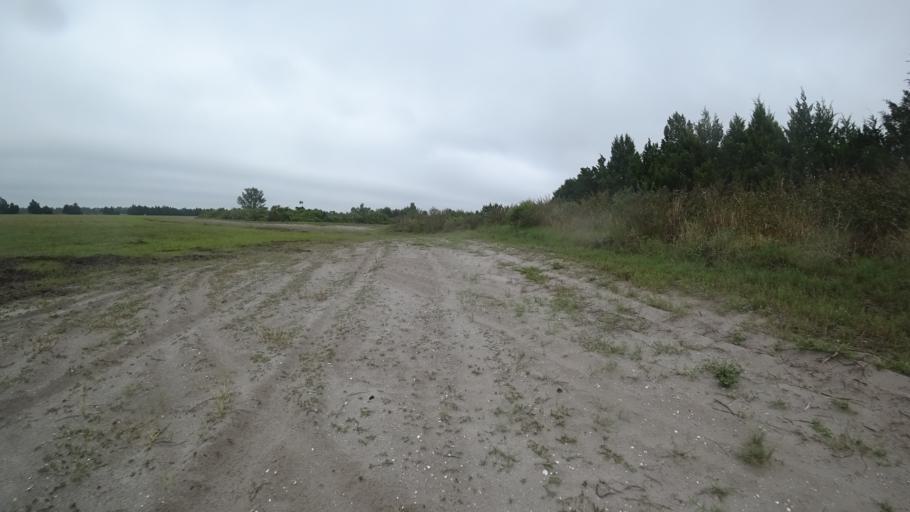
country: US
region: Florida
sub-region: Sarasota County
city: Warm Mineral Springs
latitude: 27.3054
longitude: -82.1474
